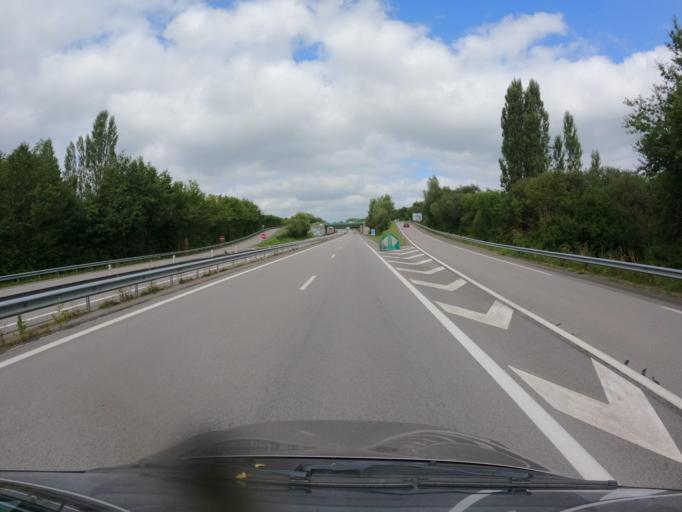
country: FR
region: Limousin
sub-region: Departement de la Haute-Vienne
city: Verneuil-sur-Vienne
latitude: 45.8532
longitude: 1.1583
